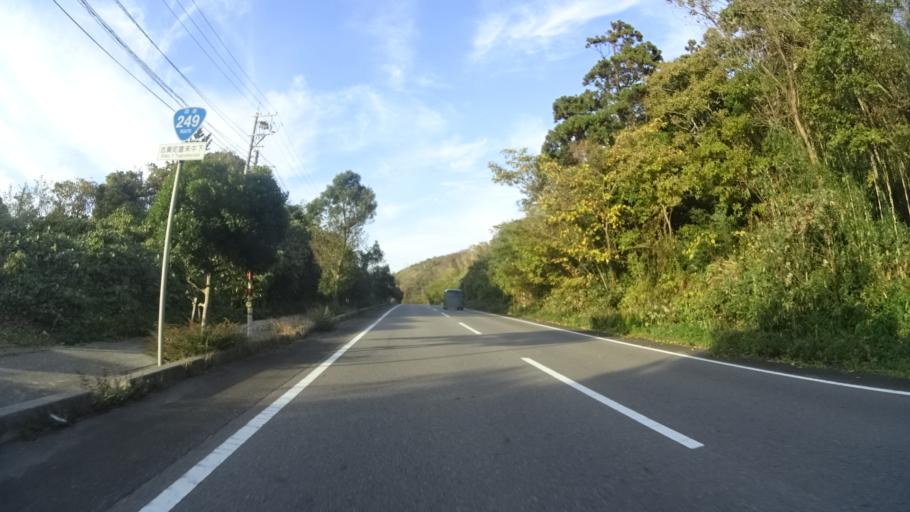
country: JP
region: Ishikawa
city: Hakui
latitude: 37.1081
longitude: 136.7284
